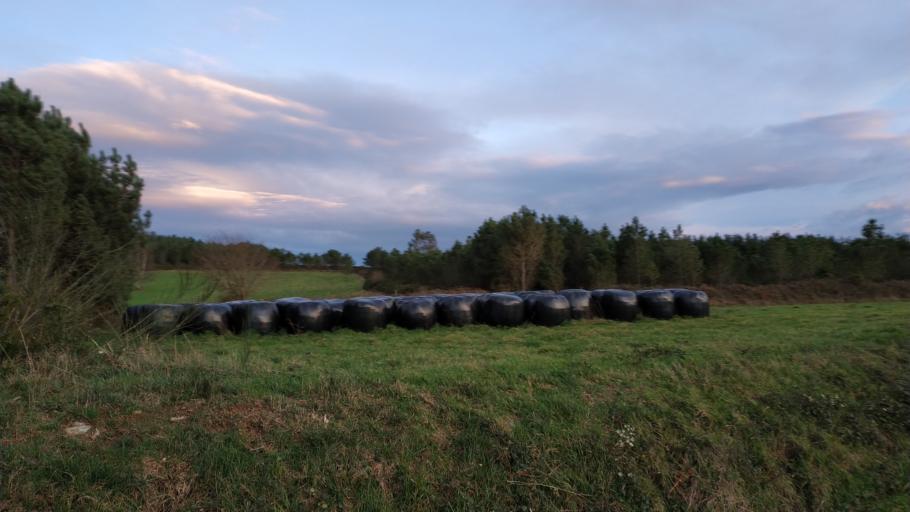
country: ES
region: Galicia
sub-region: Provincia de Pontevedra
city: Silleda
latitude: 42.7663
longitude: -8.1609
